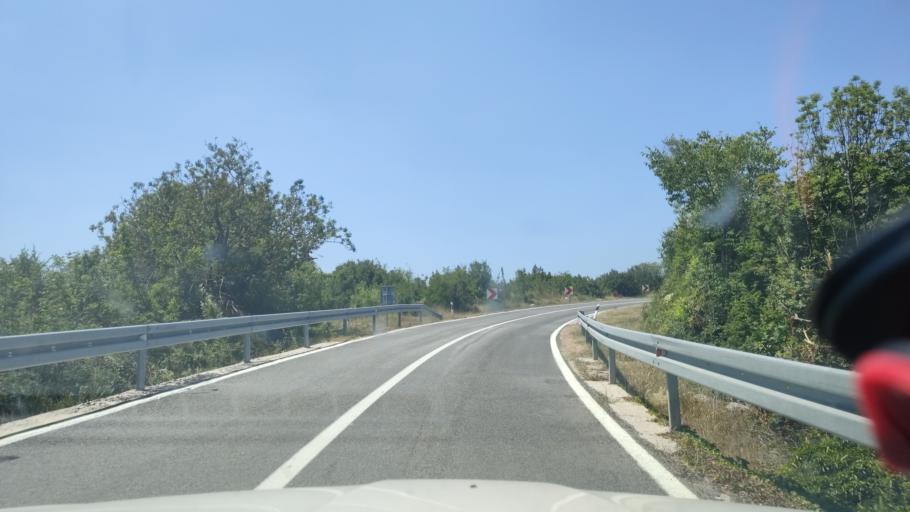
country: HR
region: Sibensko-Kniniska
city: Kistanje
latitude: 43.9759
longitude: 15.9416
